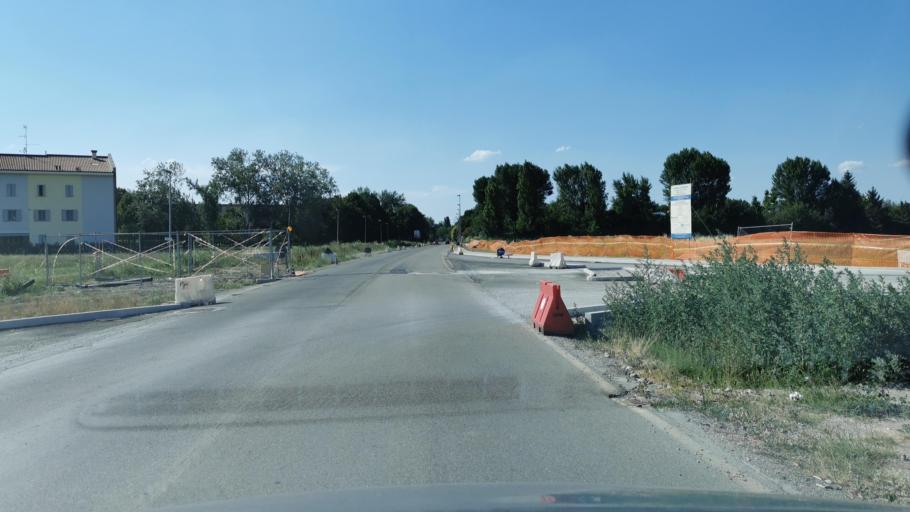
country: IT
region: Emilia-Romagna
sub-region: Provincia di Modena
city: Modena
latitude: 44.6156
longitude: 10.9344
